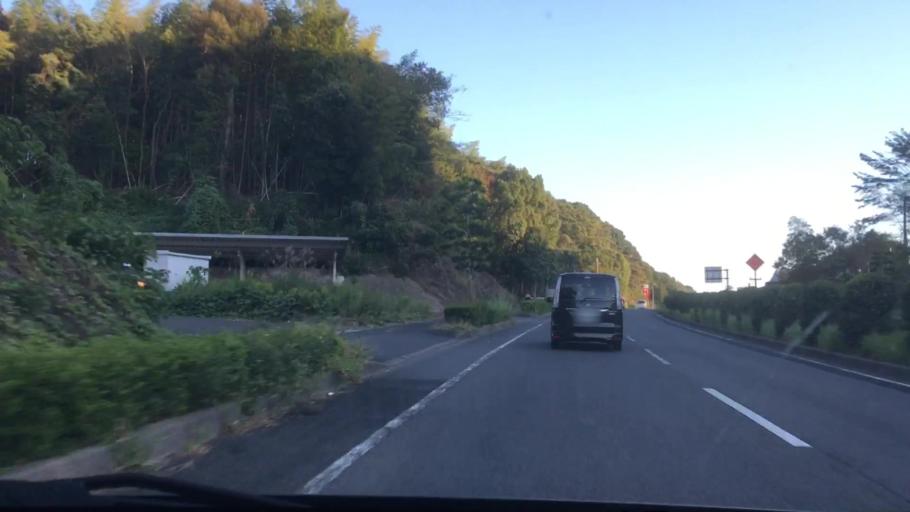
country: JP
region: Nagasaki
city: Sasebo
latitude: 33.1391
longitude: 129.7849
